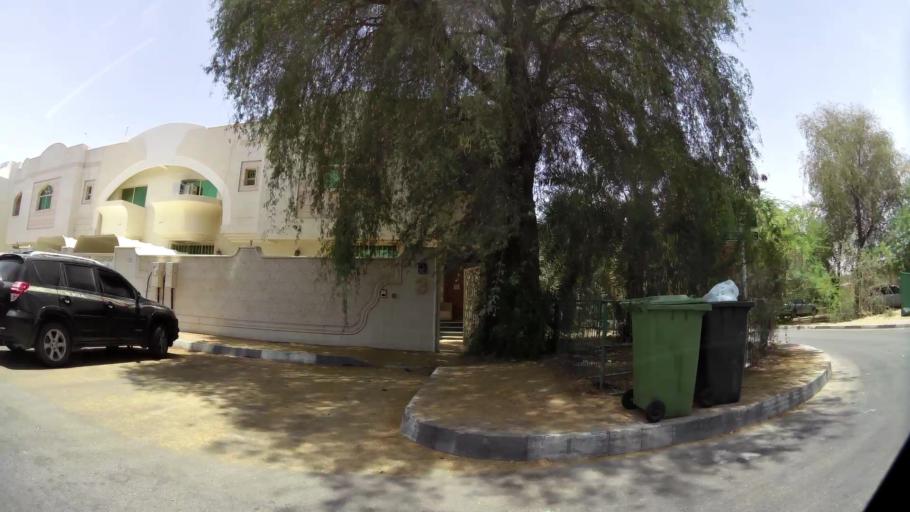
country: OM
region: Al Buraimi
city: Al Buraymi
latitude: 24.2616
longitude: 55.7328
